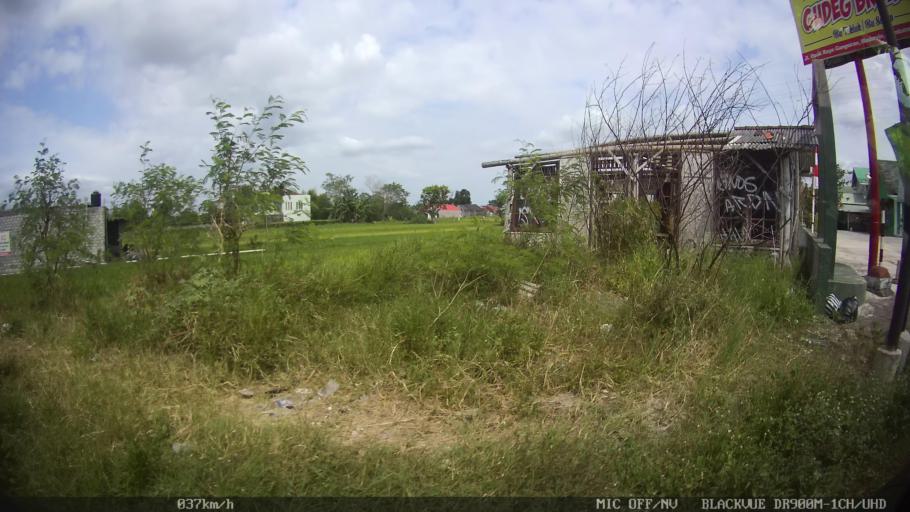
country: ID
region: Central Java
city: Candi Prambanan
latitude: -7.7858
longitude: 110.4797
